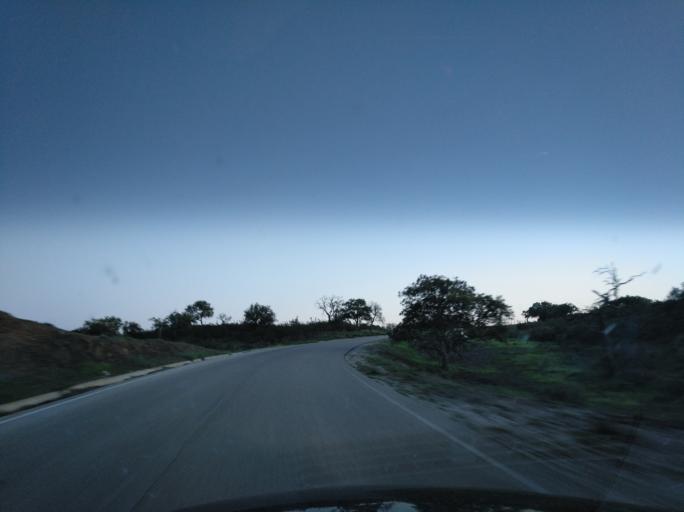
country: PT
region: Faro
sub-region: Vila Real de Santo Antonio
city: Monte Gordo
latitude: 37.2120
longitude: -7.5197
